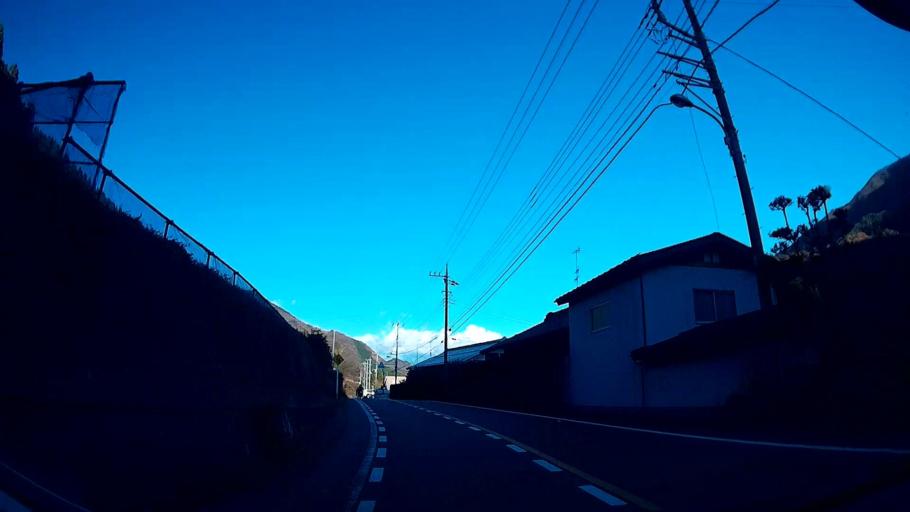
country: JP
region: Yamanashi
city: Uenohara
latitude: 35.5290
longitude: 139.0396
